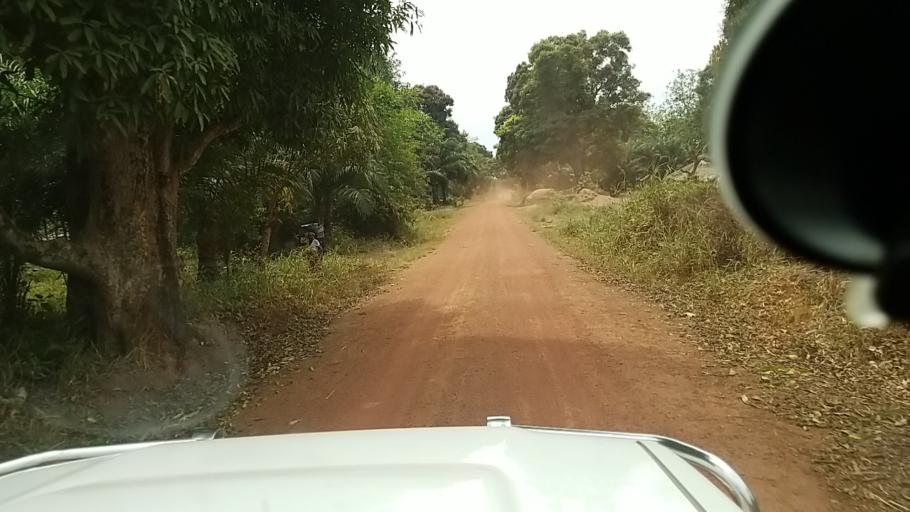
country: CD
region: Equateur
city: Libenge
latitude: 3.7325
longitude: 18.7757
